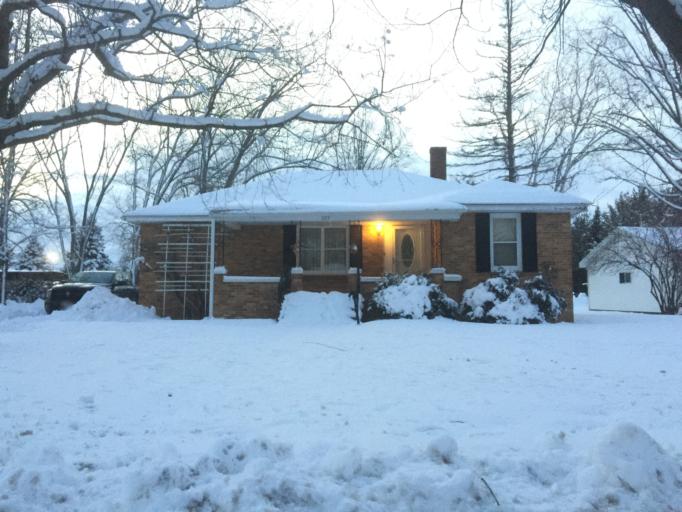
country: US
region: Wisconsin
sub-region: Marinette County
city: Peshtigo
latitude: 45.0552
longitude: -87.7606
